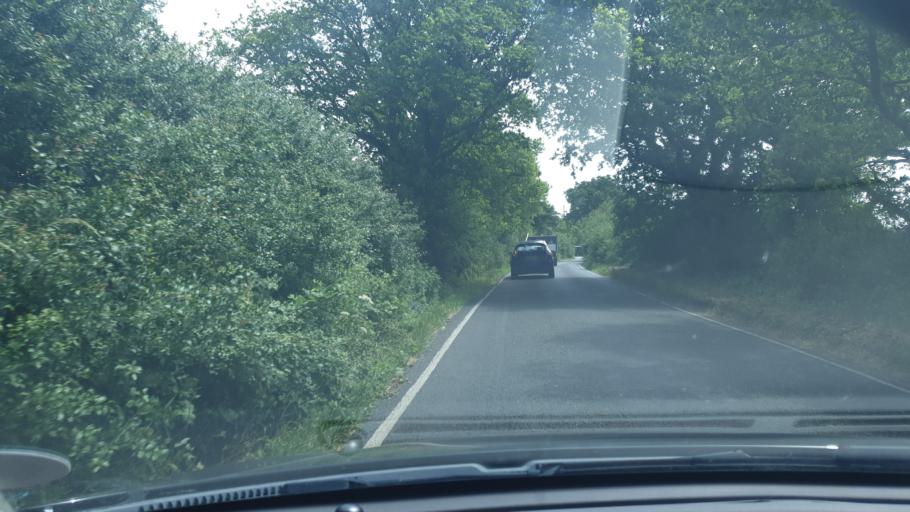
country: GB
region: England
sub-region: Essex
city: Clacton-on-Sea
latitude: 51.8119
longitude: 1.1795
